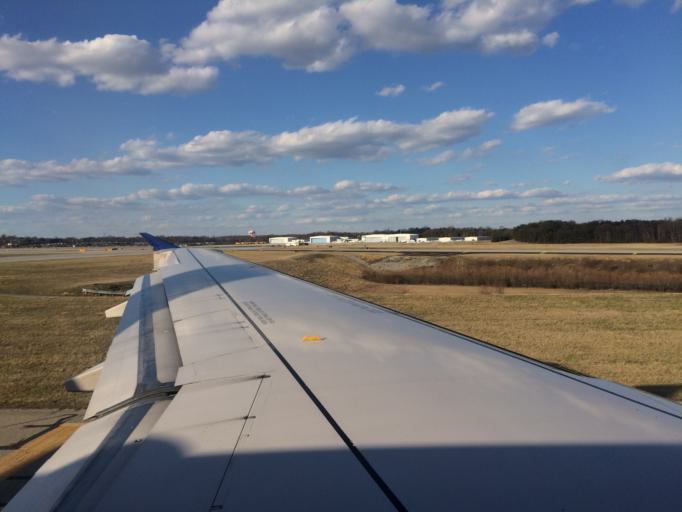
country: US
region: Maryland
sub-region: Anne Arundel County
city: Ferndale
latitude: 39.1770
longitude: -76.6612
